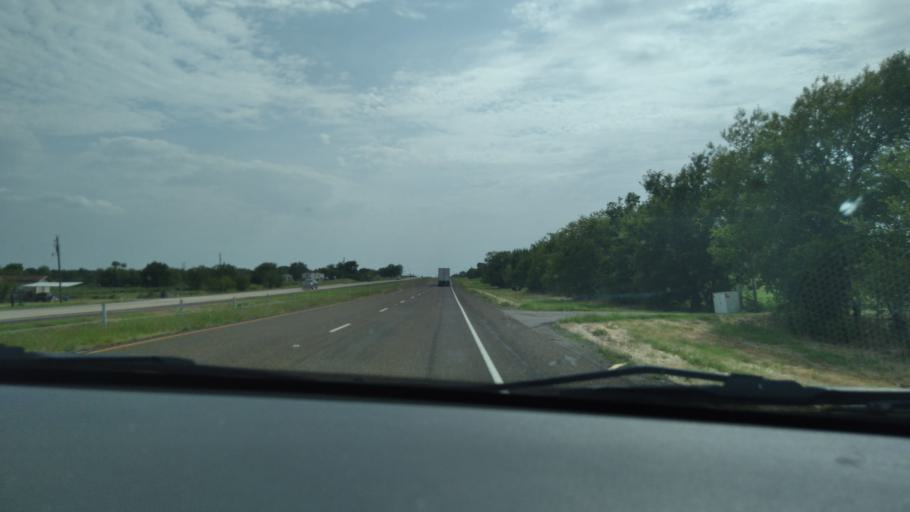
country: US
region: Texas
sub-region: Navarro County
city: Corsicana
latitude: 32.0290
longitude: -96.5636
